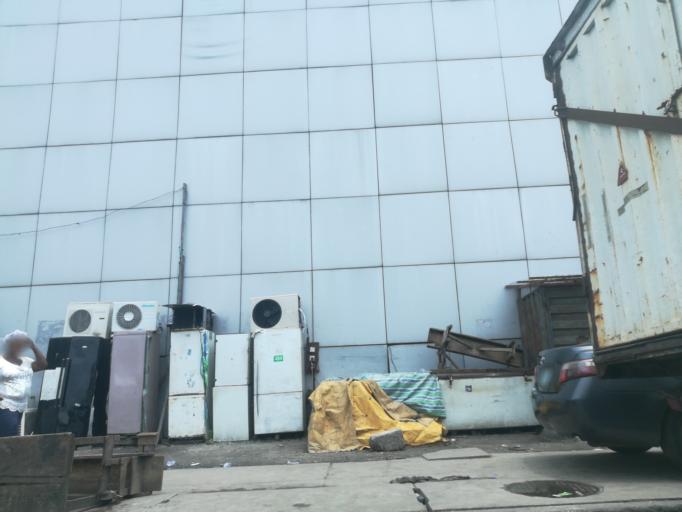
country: NG
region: Lagos
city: Lagos
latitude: 6.4566
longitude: 3.3806
